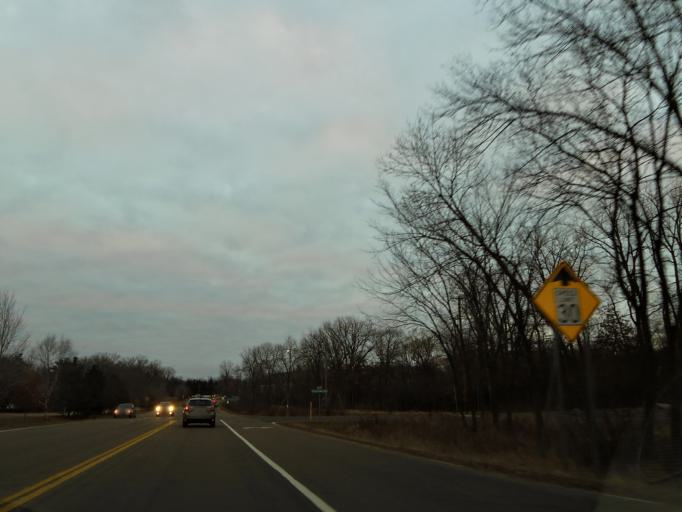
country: US
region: Minnesota
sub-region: Washington County
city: Birchwood
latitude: 45.0547
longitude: -92.9637
